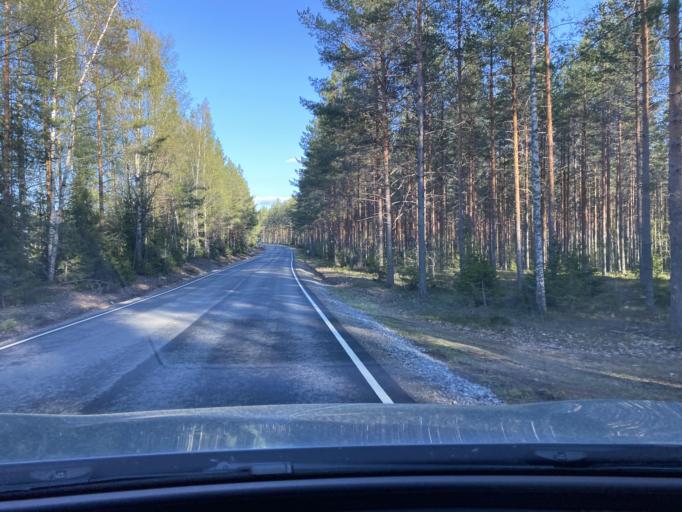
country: FI
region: Pirkanmaa
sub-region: Lounais-Pirkanmaa
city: Vammala
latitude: 61.2875
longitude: 23.0154
